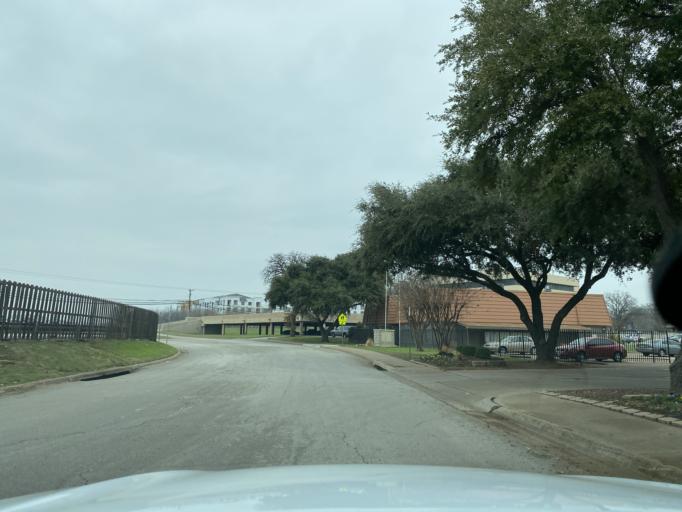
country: US
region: Texas
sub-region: Tarrant County
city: Euless
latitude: 32.8285
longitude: -97.0969
